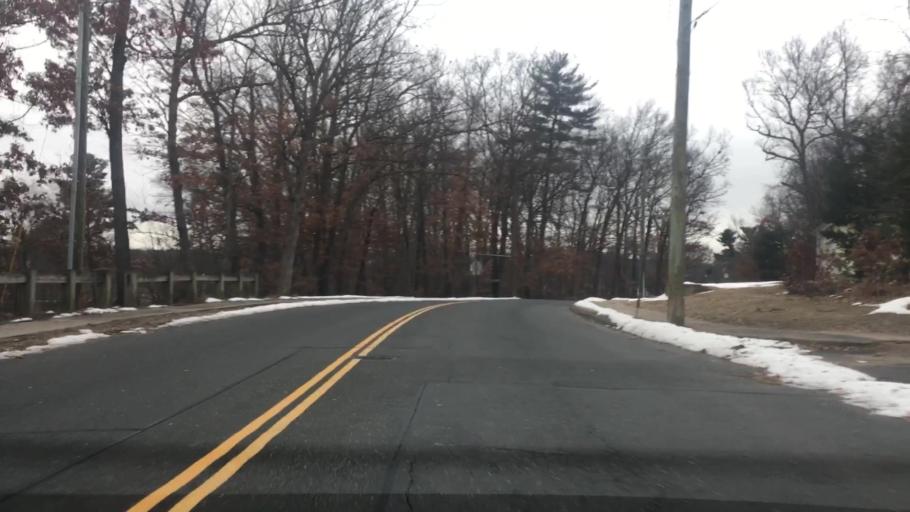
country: US
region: Connecticut
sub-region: Hartford County
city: Bristol
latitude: 41.6870
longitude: -72.9194
